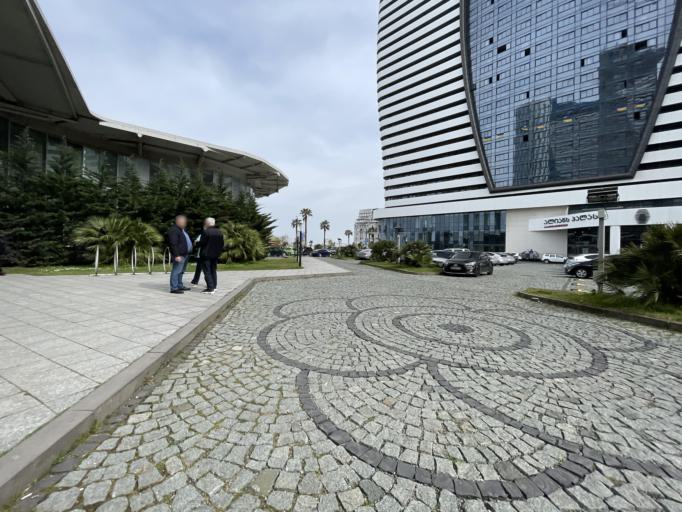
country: GE
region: Ajaria
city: Batumi
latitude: 41.6411
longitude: 41.6167
